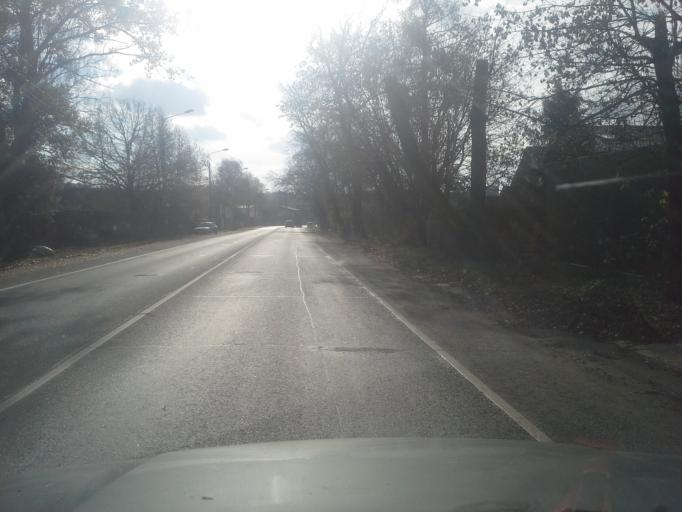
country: RU
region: Moskovskaya
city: Zvenigorod
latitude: 55.7185
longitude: 36.8654
